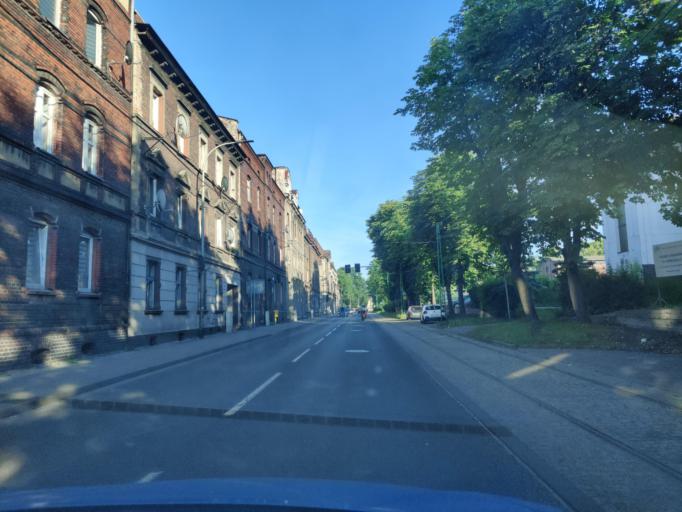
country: PL
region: Silesian Voivodeship
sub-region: Sosnowiec
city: Sosnowiec
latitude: 50.2502
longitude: 19.1306
